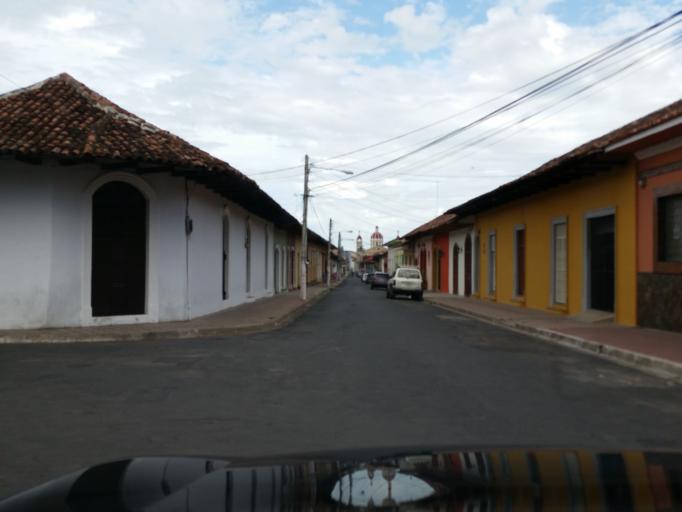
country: NI
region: Granada
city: Granada
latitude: 11.9301
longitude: -85.9591
